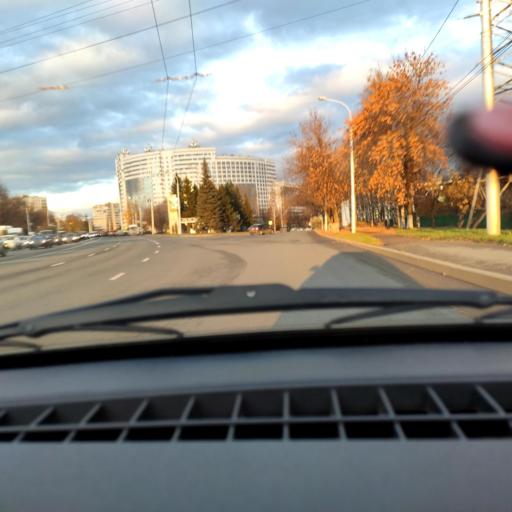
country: RU
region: Bashkortostan
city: Ufa
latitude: 54.8092
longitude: 56.0534
